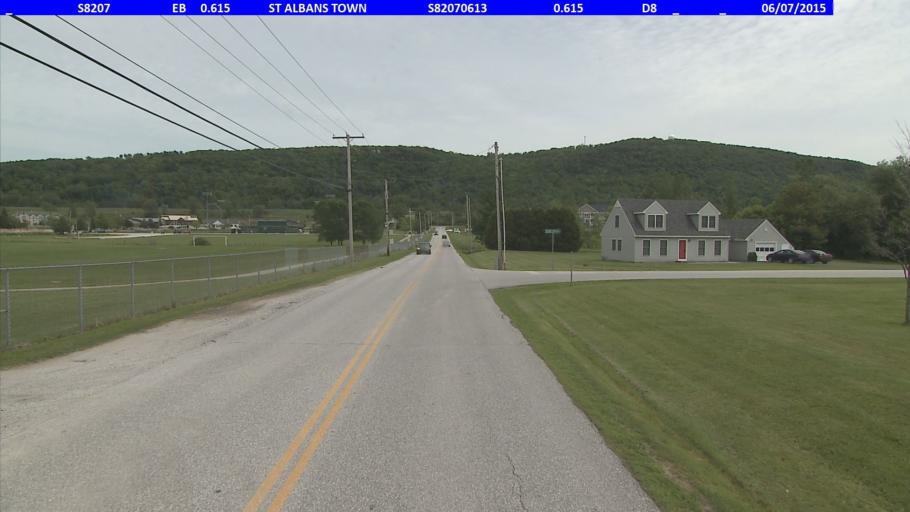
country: US
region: Vermont
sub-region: Franklin County
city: Saint Albans
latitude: 44.7927
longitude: -73.0803
